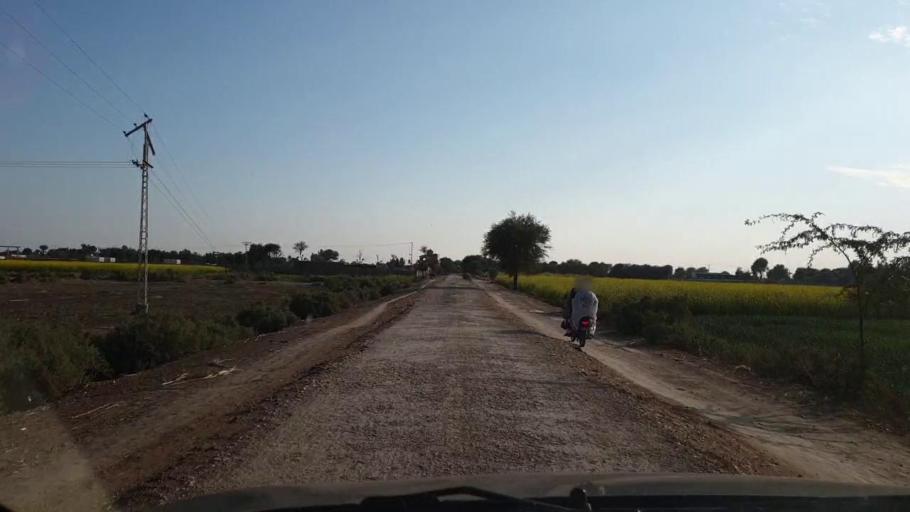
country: PK
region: Sindh
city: Jhol
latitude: 25.9531
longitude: 68.8615
